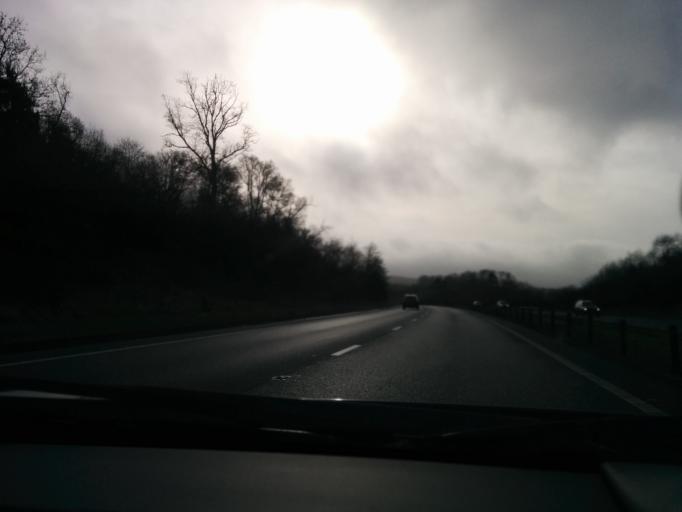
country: GB
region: England
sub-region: West Berkshire
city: Newbury
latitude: 51.4095
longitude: -1.3550
